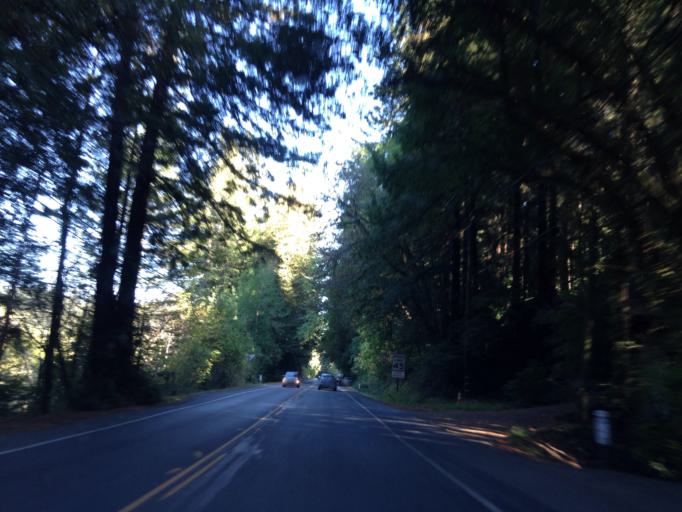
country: US
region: California
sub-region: Sonoma County
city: Monte Rio
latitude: 38.4823
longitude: -123.0105
